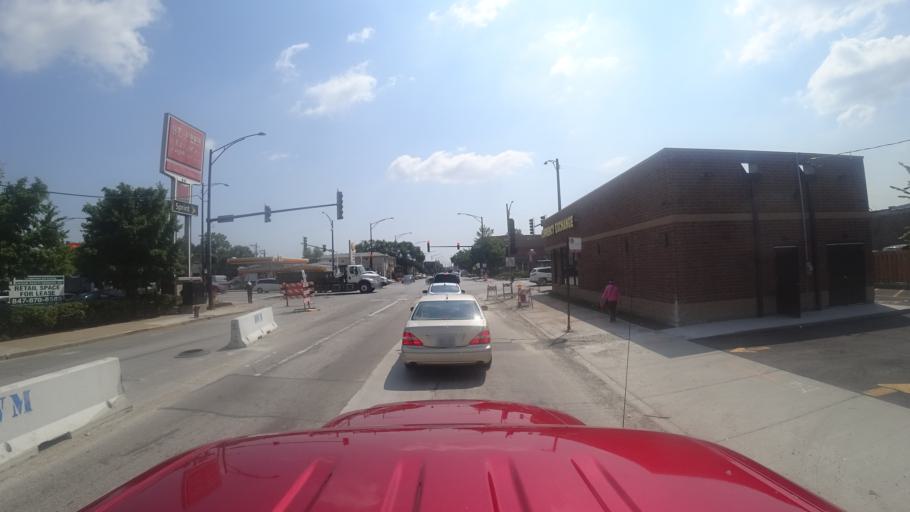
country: US
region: Illinois
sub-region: Cook County
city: Cicero
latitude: 41.8079
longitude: -87.7241
